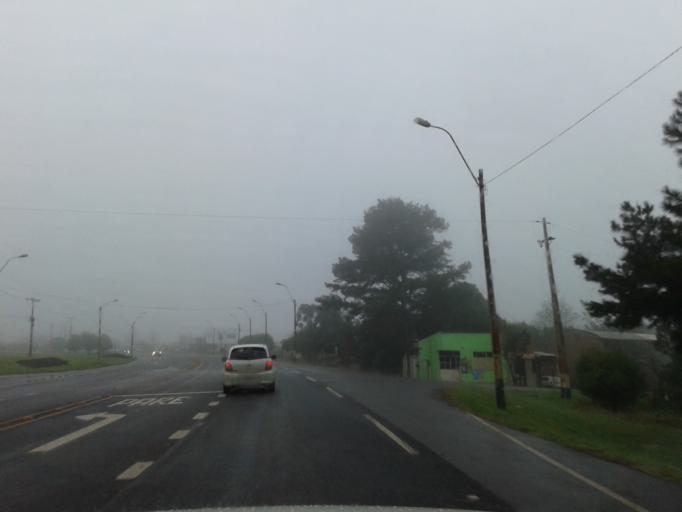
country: PY
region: Itapua
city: Arquitecto Tomas Romero Pereira
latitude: -26.5478
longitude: -55.2579
